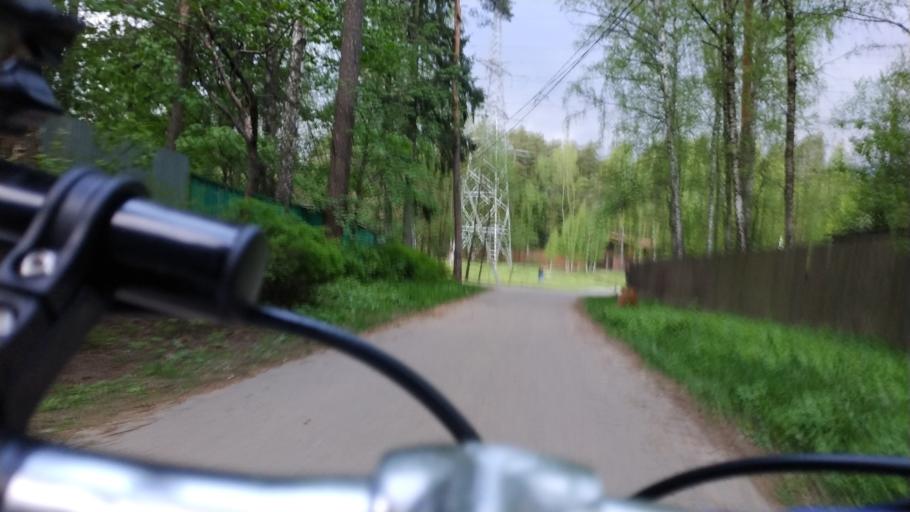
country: RU
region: Moskovskaya
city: Kratovo
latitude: 55.6092
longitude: 38.1566
